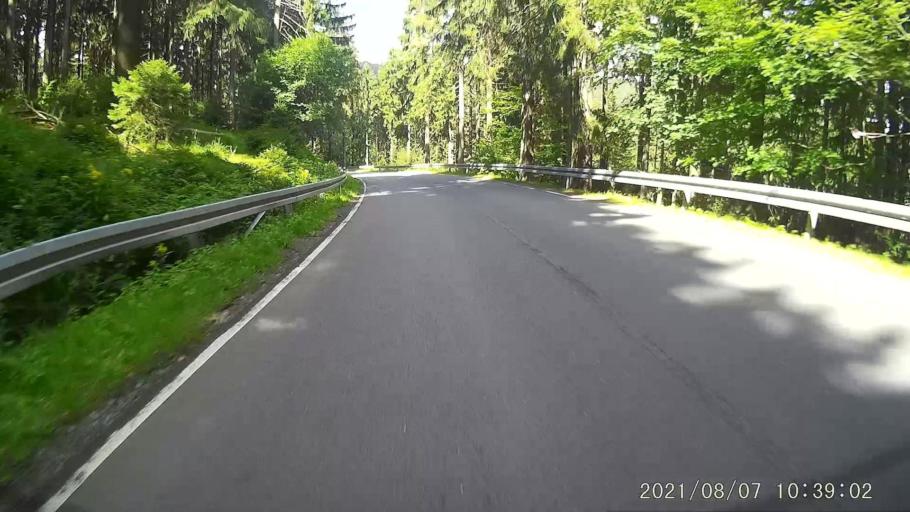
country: PL
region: Lower Silesian Voivodeship
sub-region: Powiat klodzki
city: Duszniki-Zdroj
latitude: 50.3516
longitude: 16.3769
